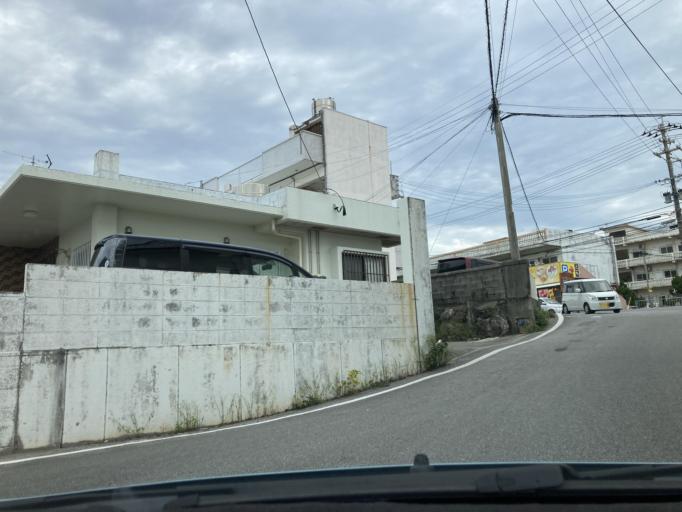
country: JP
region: Okinawa
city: Okinawa
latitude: 26.3833
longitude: 127.7419
